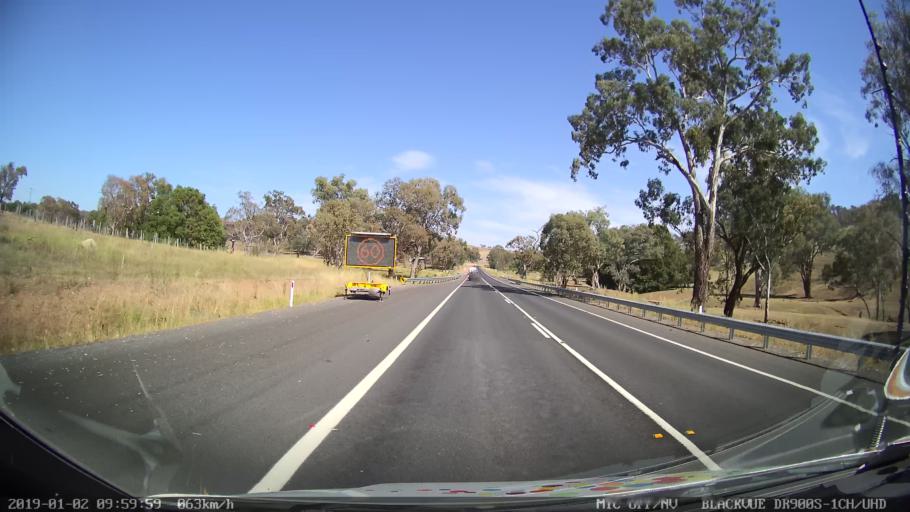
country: AU
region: New South Wales
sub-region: Gundagai
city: Gundagai
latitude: -35.1970
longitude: 148.1365
